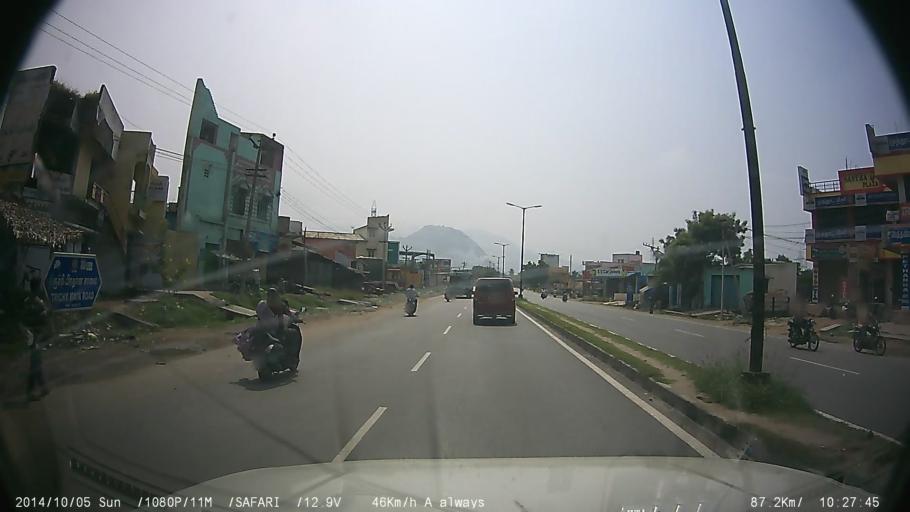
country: IN
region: Tamil Nadu
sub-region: Salem
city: Salem
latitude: 11.6321
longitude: 78.1282
